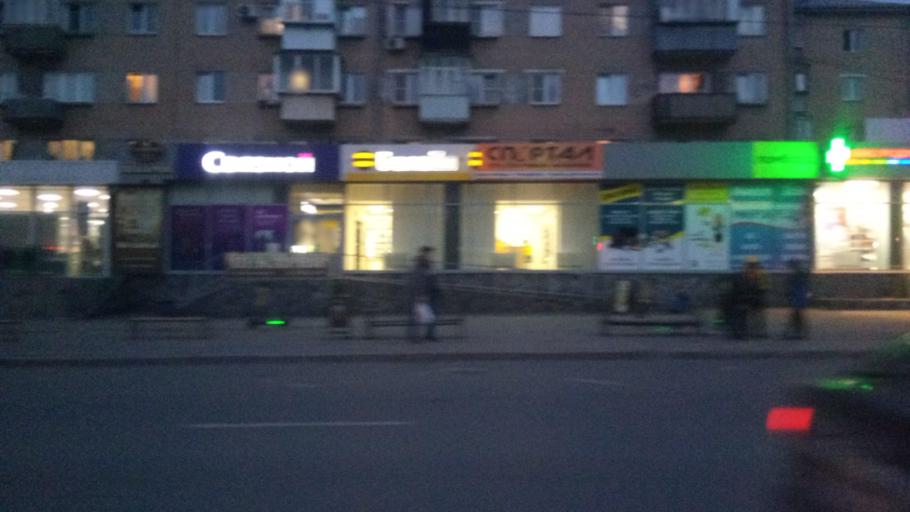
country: RU
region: Chelyabinsk
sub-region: Gorod Chelyabinsk
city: Chelyabinsk
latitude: 55.1706
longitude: 61.4628
